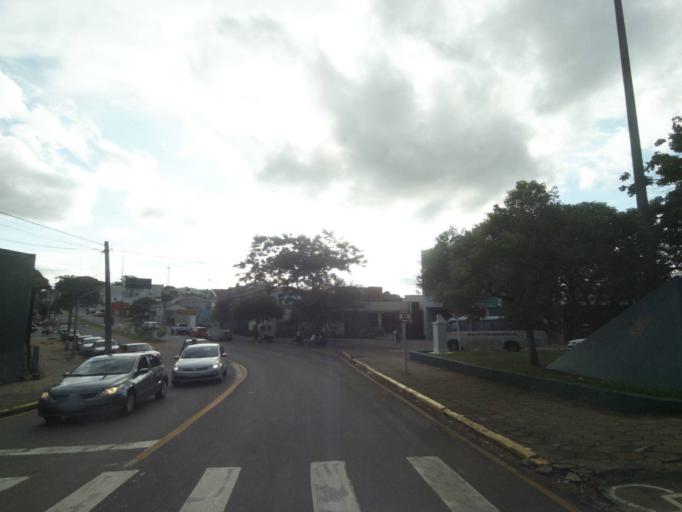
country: BR
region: Parana
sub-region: Telemaco Borba
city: Telemaco Borba
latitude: -24.3262
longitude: -50.6169
